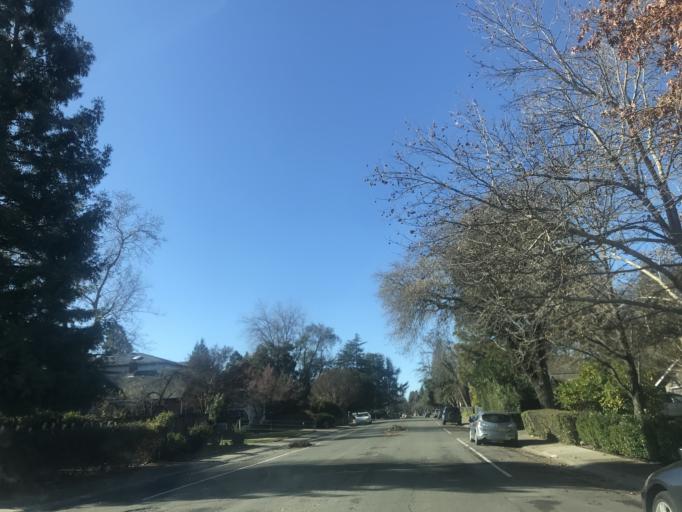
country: US
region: California
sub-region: Sacramento County
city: Sacramento
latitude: 38.5315
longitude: -121.4975
